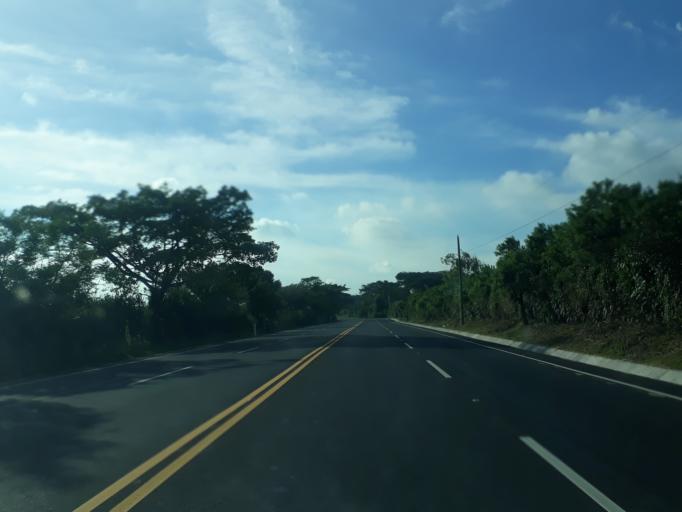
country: NI
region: Carazo
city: Diriamba
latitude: 11.9130
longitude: -86.2687
